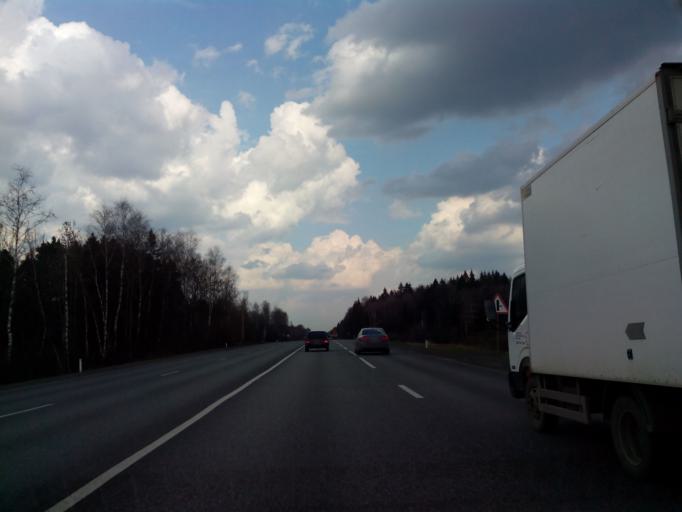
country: RU
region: Moskovskaya
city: Dorokhovo
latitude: 55.5335
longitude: 36.3716
